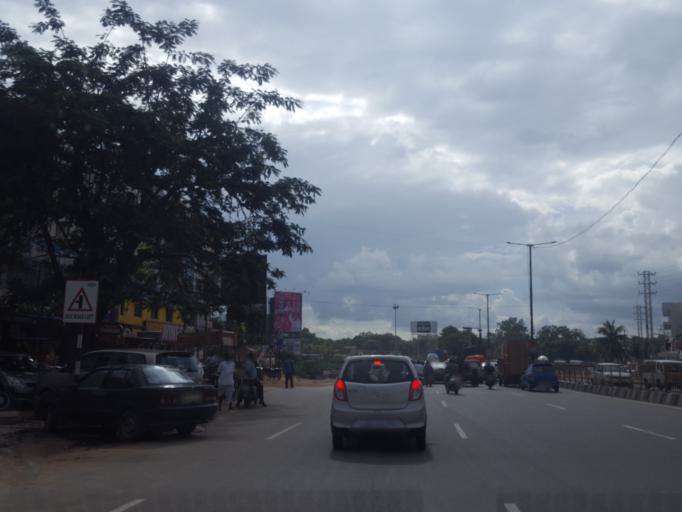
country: IN
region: Telangana
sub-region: Medak
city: Serilingampalle
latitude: 17.4950
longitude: 78.3184
